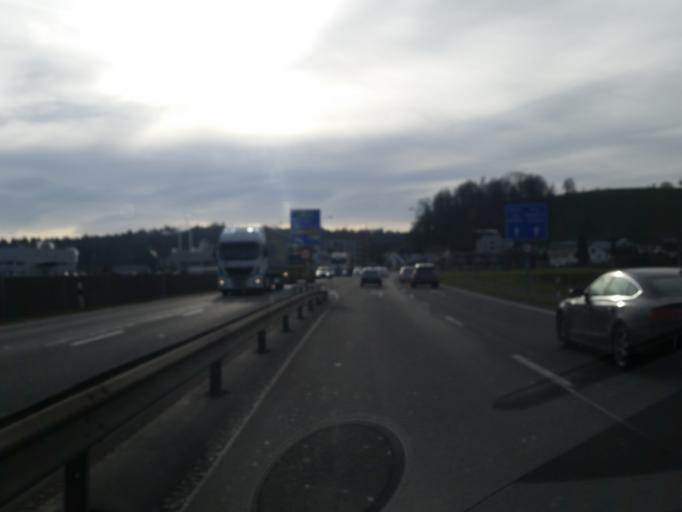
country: CH
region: Aargau
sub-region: Bezirk Lenzburg
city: Niederlenz
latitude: 47.3941
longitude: 8.1914
